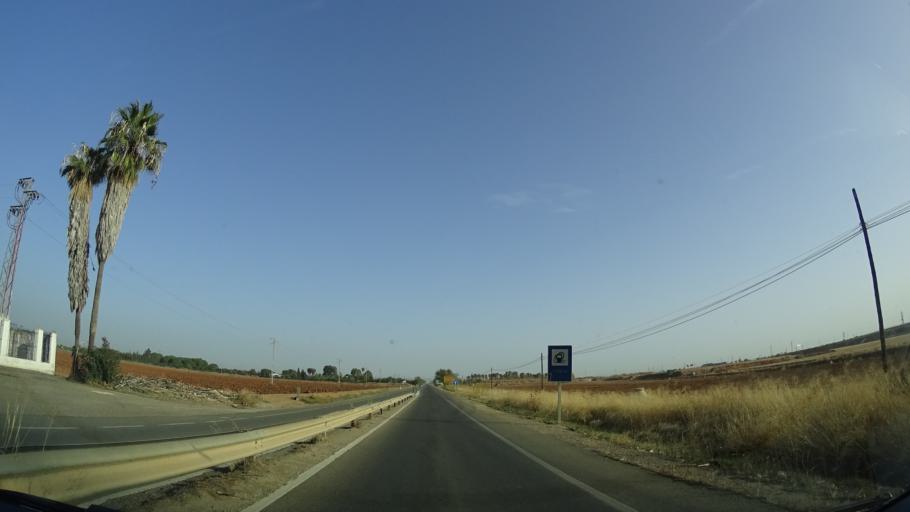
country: ES
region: Andalusia
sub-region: Provincia de Sevilla
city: La Algaba
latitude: 37.4362
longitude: -5.9792
